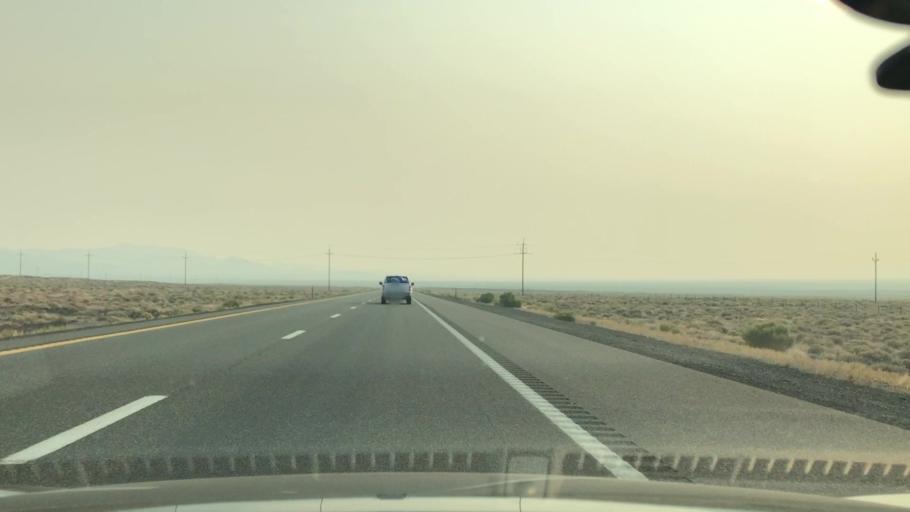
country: US
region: Nevada
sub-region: Churchill County
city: Fallon
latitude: 39.8926
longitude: -118.8527
